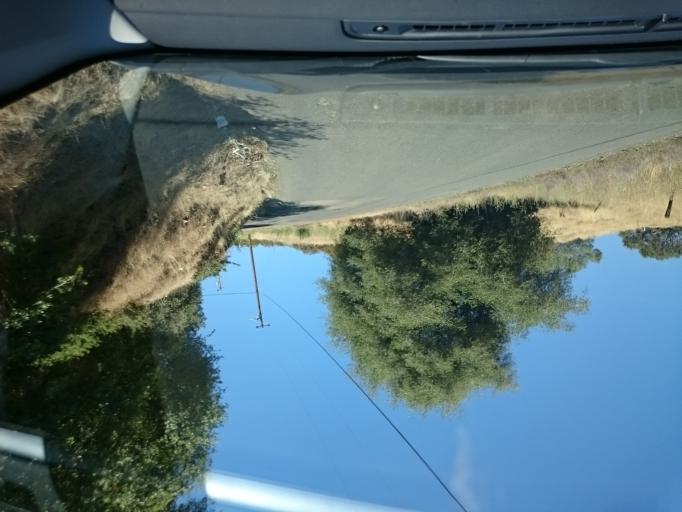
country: US
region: California
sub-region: Calaveras County
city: Rancho Calaveras
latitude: 38.1247
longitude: -120.8094
